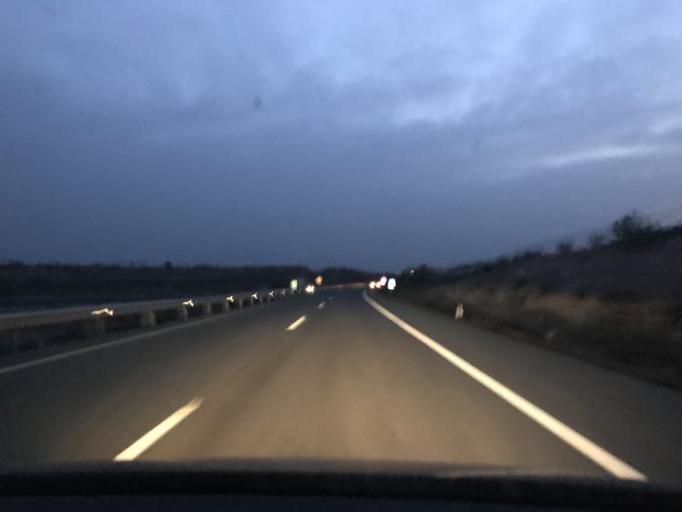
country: ES
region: Andalusia
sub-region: Provincia de Granada
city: Gor
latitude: 37.3945
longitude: -2.9706
